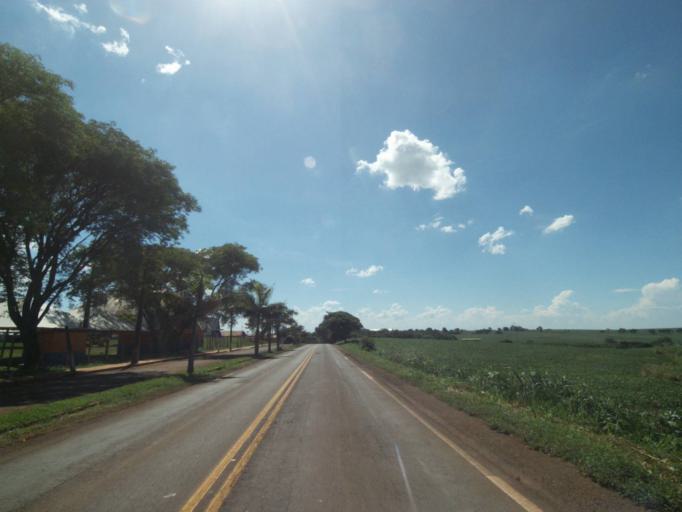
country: BR
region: Parana
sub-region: Sertanopolis
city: Sertanopolis
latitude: -23.0343
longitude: -50.8124
